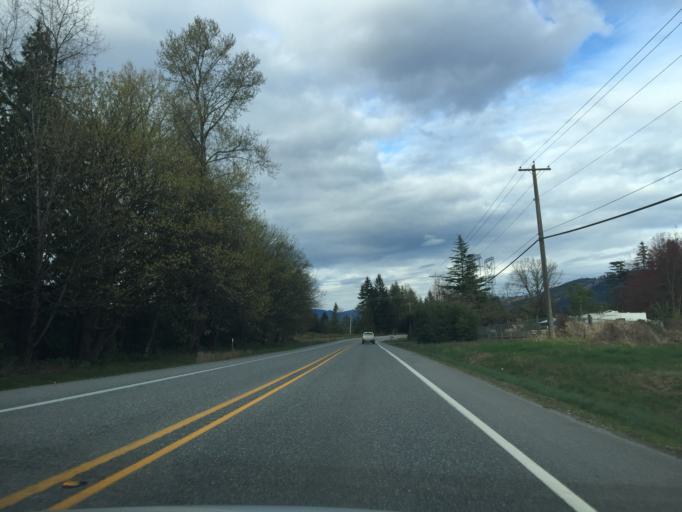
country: US
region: Washington
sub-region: Snohomish County
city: Arlington
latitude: 48.2244
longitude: -122.1012
